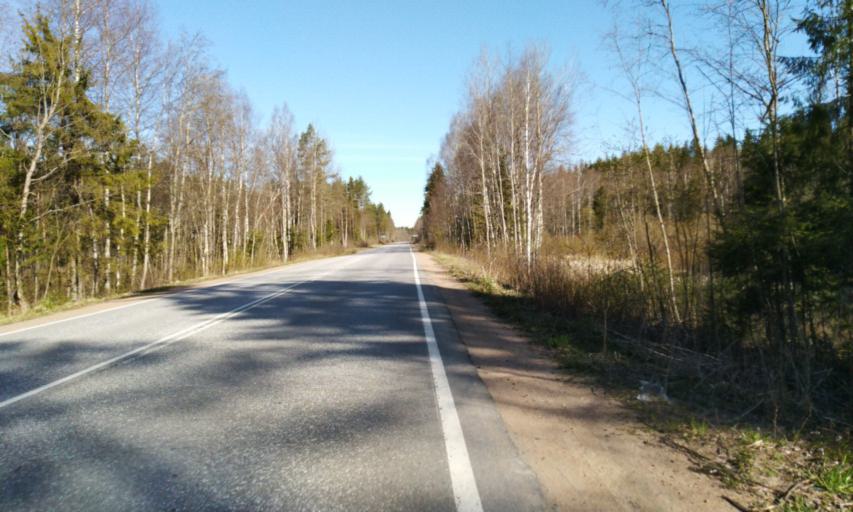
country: RU
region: Leningrad
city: Garbolovo
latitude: 60.3322
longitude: 30.4419
